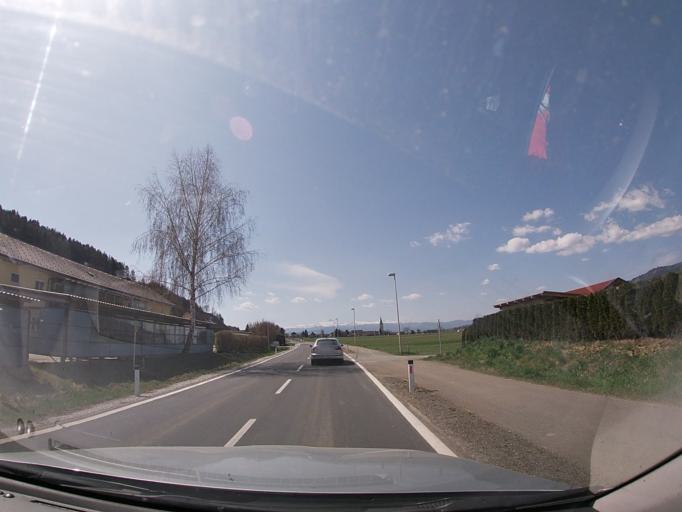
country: AT
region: Styria
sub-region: Politischer Bezirk Murtal
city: Sankt Margarethen bei Knittelfeld
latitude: 47.2321
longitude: 14.8654
